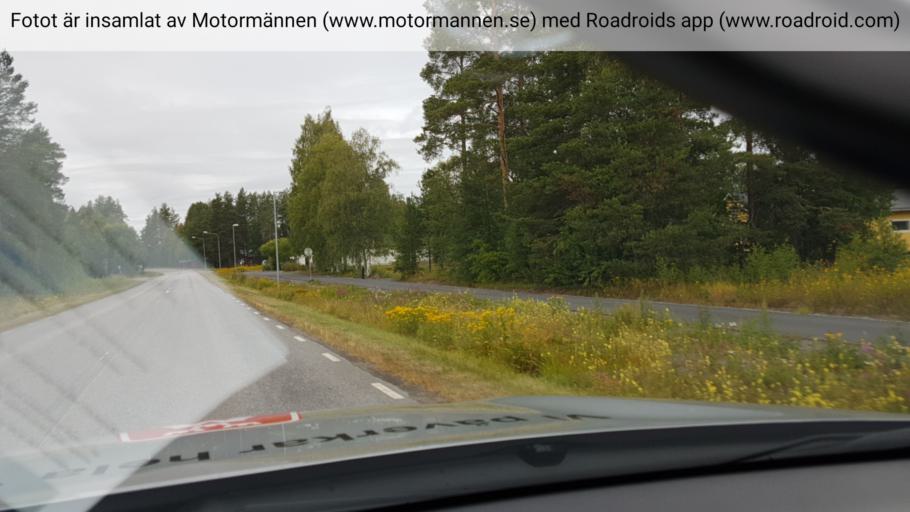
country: SE
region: Norrbotten
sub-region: Bodens Kommun
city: Boden
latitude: 65.8148
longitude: 21.6188
